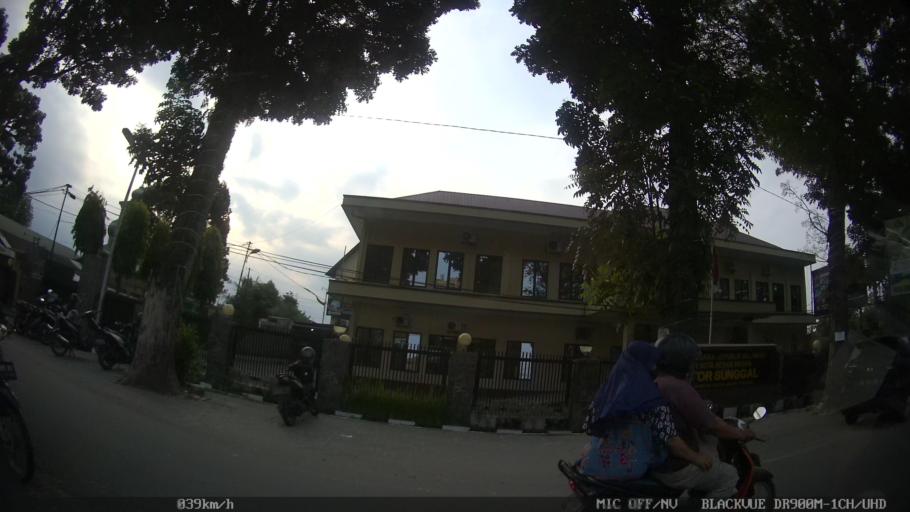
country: ID
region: North Sumatra
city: Sunggal
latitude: 3.5804
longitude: 98.6142
